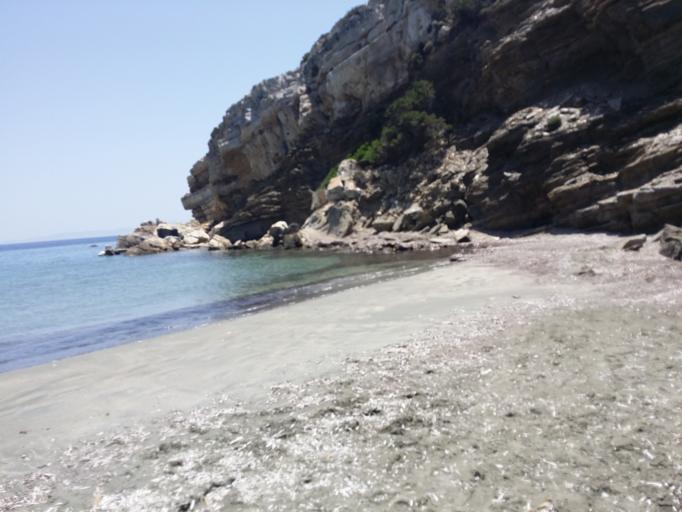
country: GR
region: South Aegean
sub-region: Nomos Kykladon
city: Antiparos
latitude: 36.9550
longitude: 24.9994
